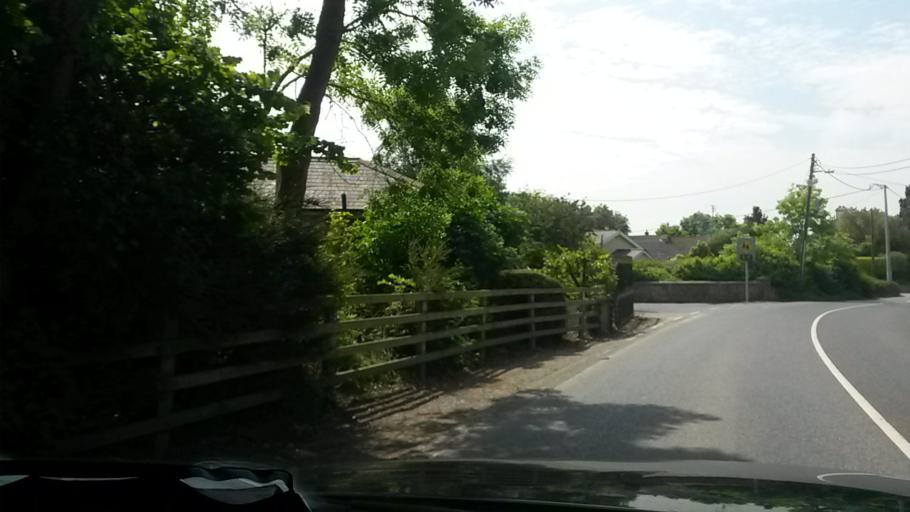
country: IE
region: Leinster
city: Donabate
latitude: 53.4924
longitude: -6.1331
